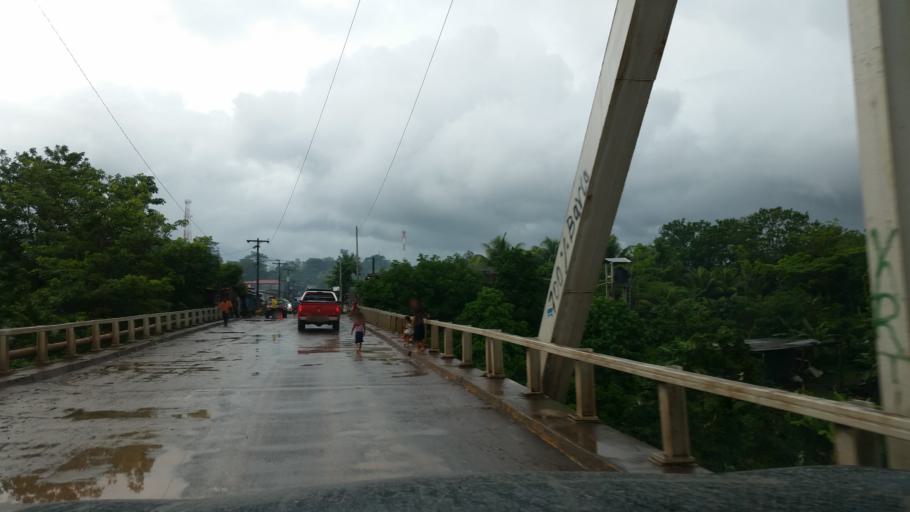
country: NI
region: Matagalpa
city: Rio Blanco
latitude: 13.1725
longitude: -84.9584
